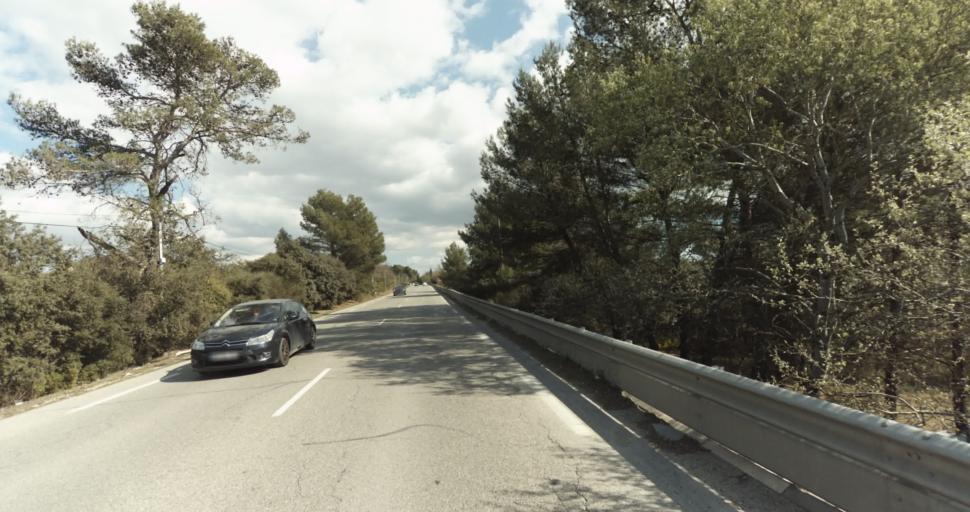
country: FR
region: Provence-Alpes-Cote d'Azur
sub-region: Departement des Bouches-du-Rhone
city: Greasque
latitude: 43.4465
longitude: 5.5163
